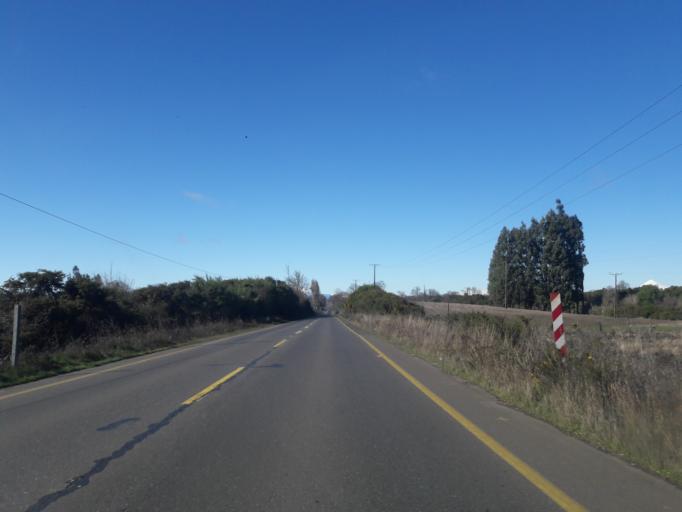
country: CL
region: Araucania
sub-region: Provincia de Malleco
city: Victoria
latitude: -38.2572
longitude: -72.2657
